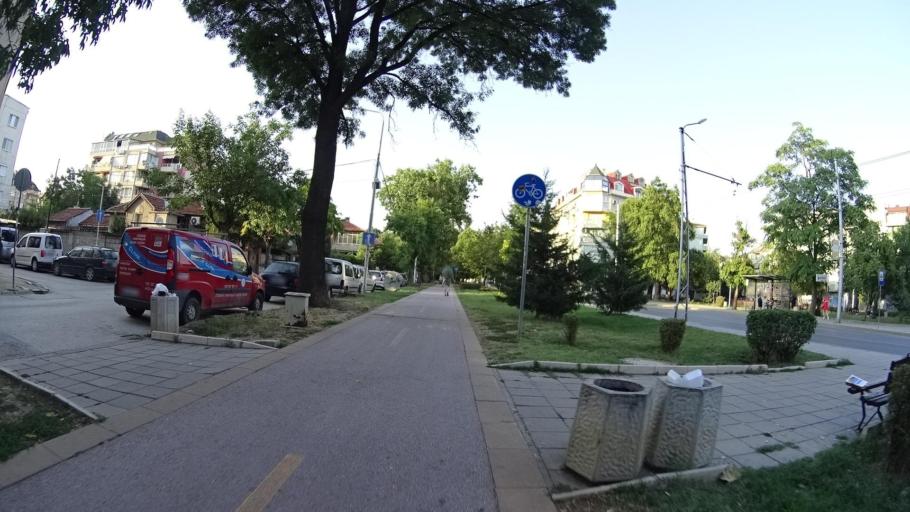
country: BG
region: Plovdiv
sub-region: Obshtina Plovdiv
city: Plovdiv
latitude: 42.1282
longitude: 24.7428
